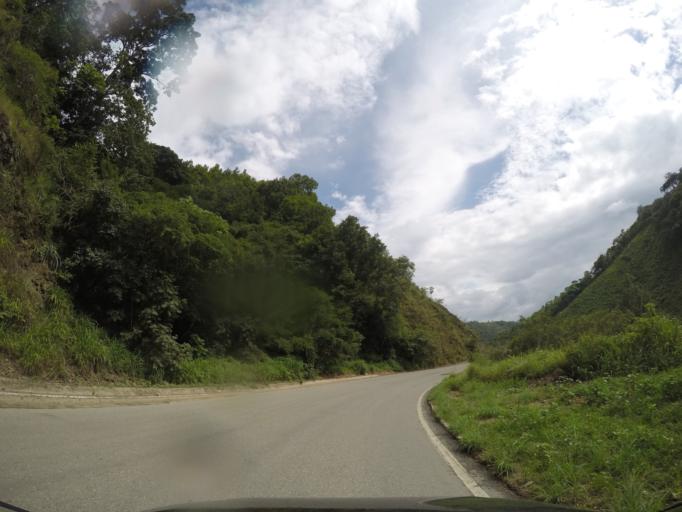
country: MX
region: Oaxaca
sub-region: San Jeronimo Coatlan
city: San Cristobal Honduras
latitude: 16.3843
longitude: -97.0756
